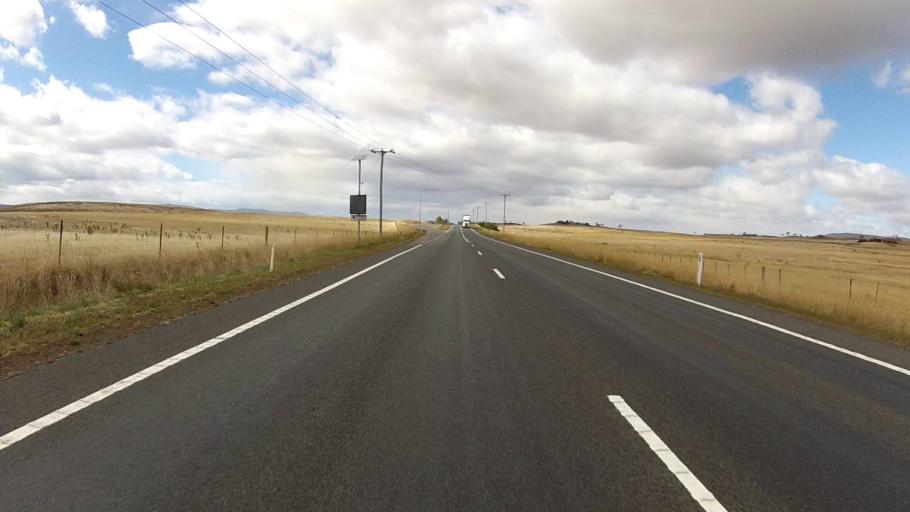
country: AU
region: Tasmania
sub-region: Northern Midlands
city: Evandale
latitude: -41.8814
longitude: 147.4652
